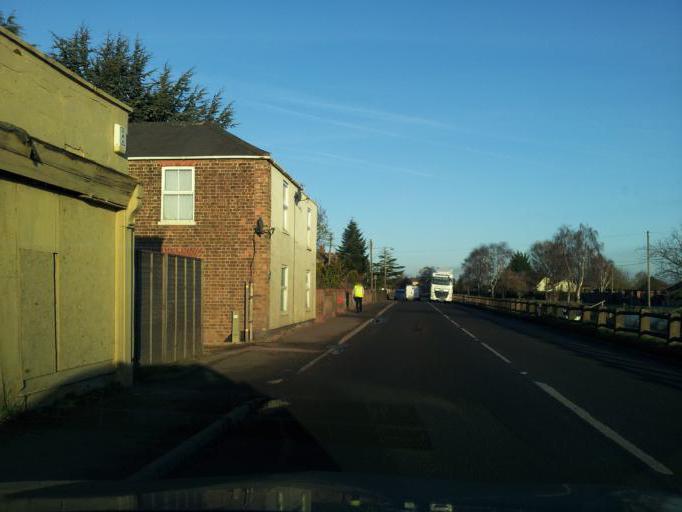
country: GB
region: England
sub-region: Norfolk
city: Outwell
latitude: 52.6055
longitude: 0.2270
